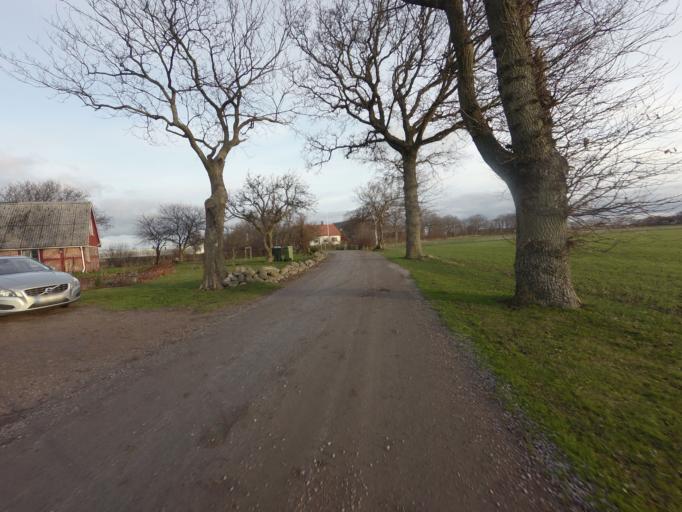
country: SE
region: Skane
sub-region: Hoganas Kommun
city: Hoganas
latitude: 56.1704
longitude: 12.5817
